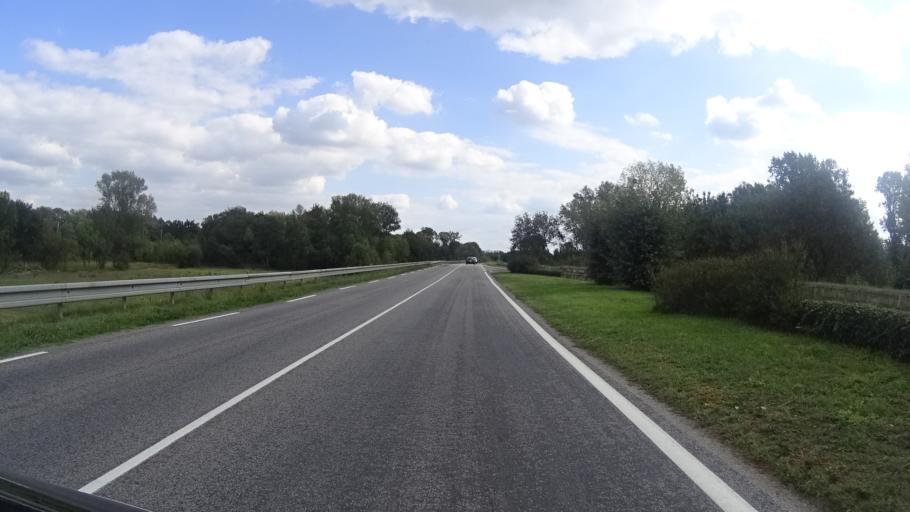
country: FR
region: Pays de la Loire
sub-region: Departement de Maine-et-Loire
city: Saint-Martin-de-la-Place
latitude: 47.3101
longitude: -0.1401
